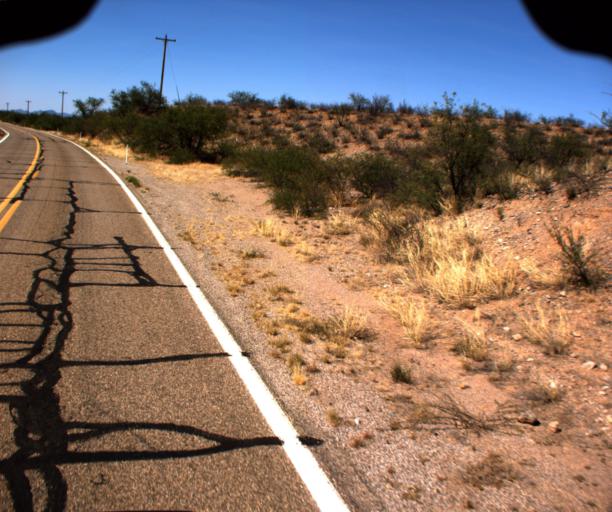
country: US
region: Arizona
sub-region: Pima County
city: Three Points
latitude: 31.8750
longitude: -111.3952
